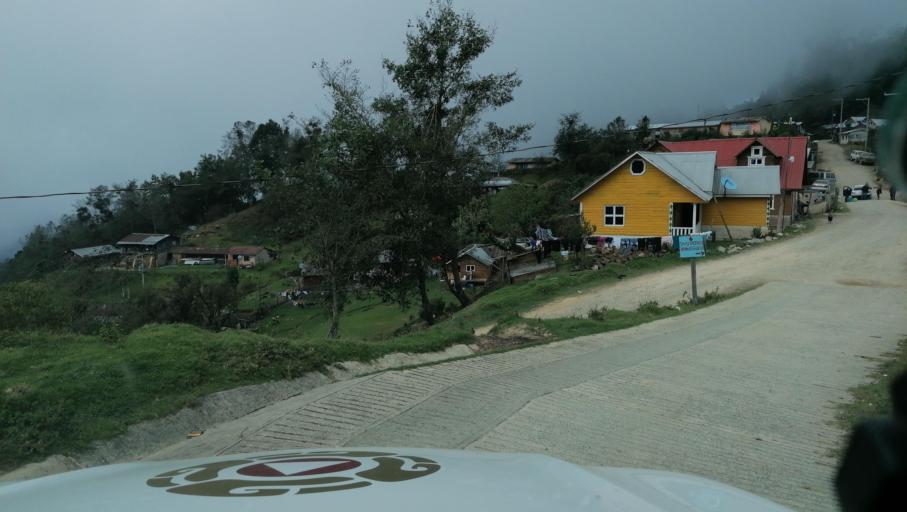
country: MX
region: Chiapas
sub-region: Tapachula
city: Canton Villaflor
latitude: 15.2060
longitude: -92.2386
